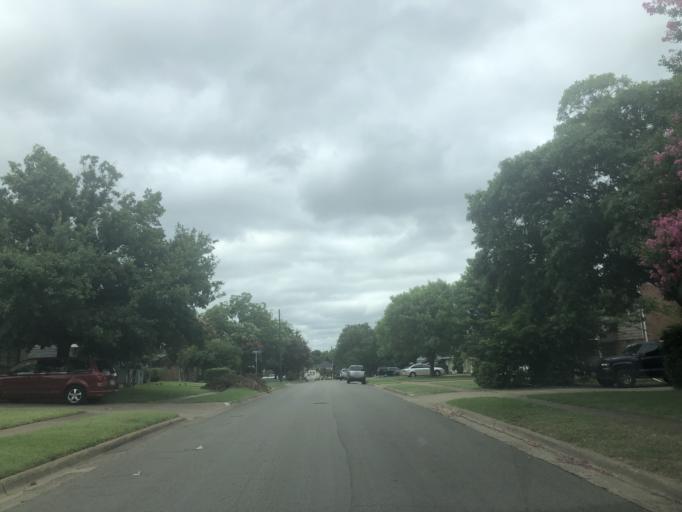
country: US
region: Texas
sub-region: Dallas County
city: Duncanville
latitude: 32.6534
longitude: -96.9168
